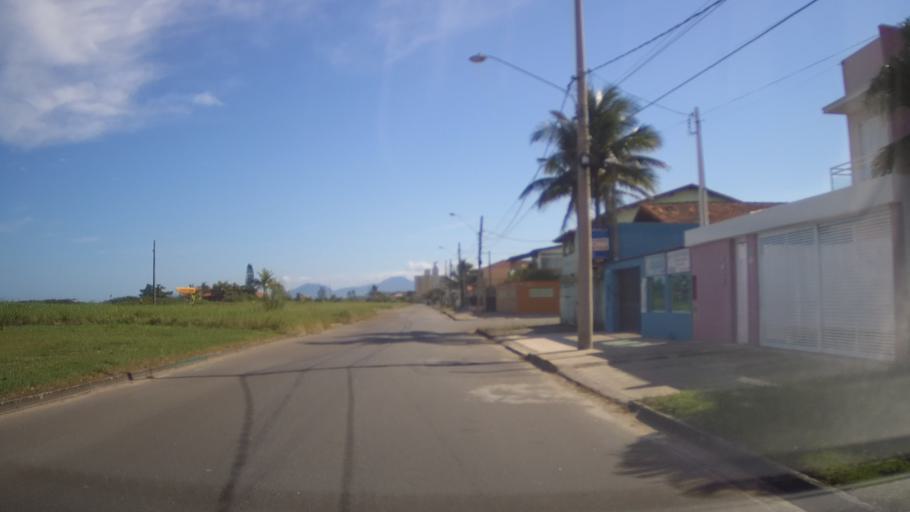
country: BR
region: Sao Paulo
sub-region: Itanhaem
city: Itanhaem
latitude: -24.2106
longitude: -46.8351
